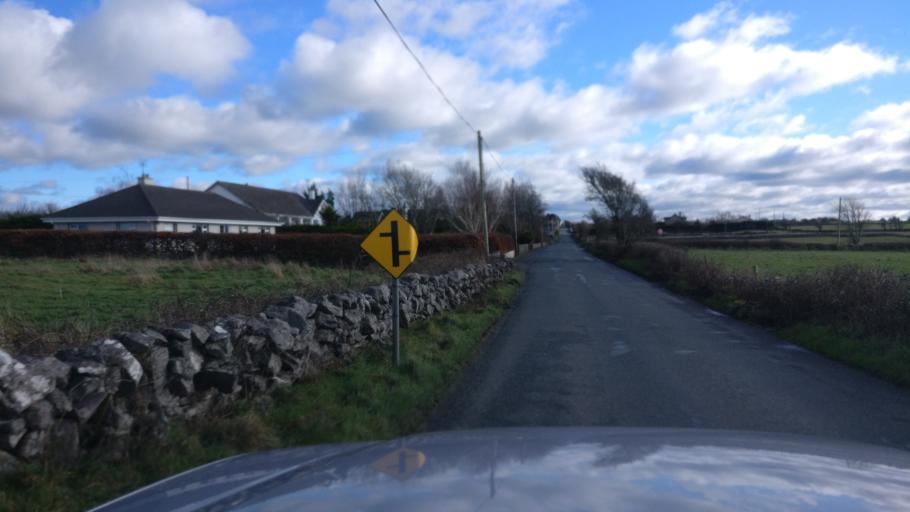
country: IE
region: Connaught
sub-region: County Galway
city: Oranmore
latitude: 53.2671
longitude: -8.8723
